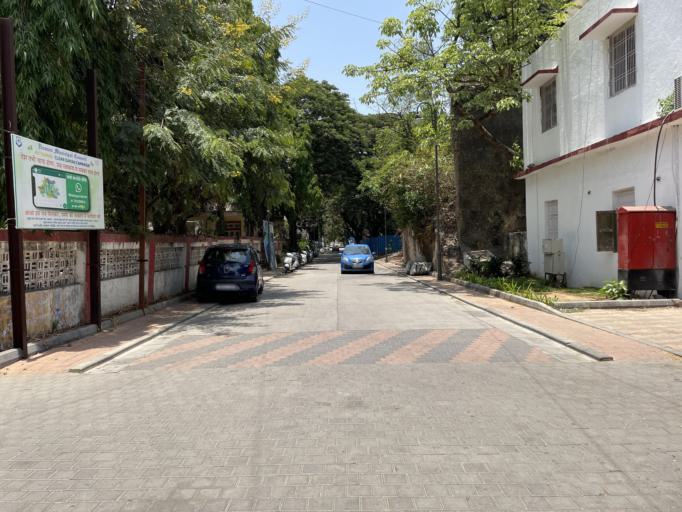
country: IN
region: Daman and Diu
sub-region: Daman District
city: Daman
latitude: 20.4080
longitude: 72.8329
